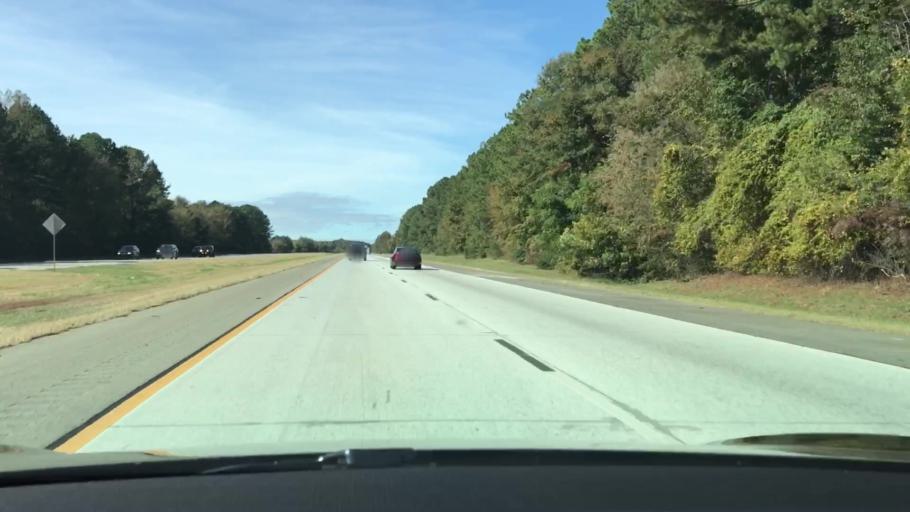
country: US
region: Georgia
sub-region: Morgan County
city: Madison
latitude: 33.5543
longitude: -83.3959
